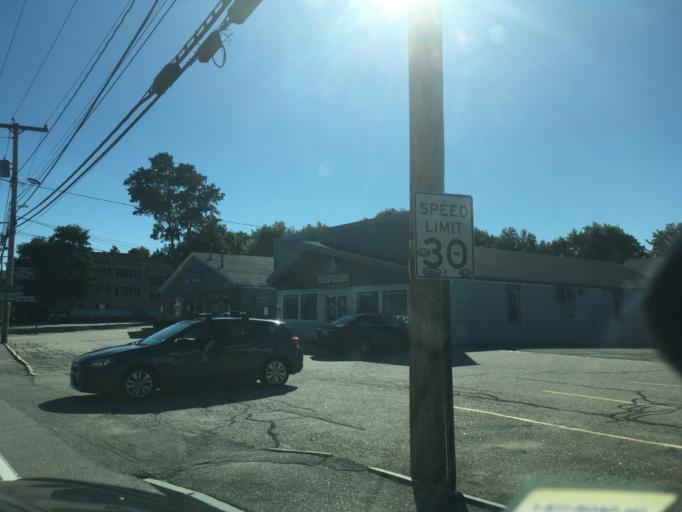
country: US
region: New Hampshire
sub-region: Rockingham County
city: Exeter
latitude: 42.9826
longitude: -70.9401
